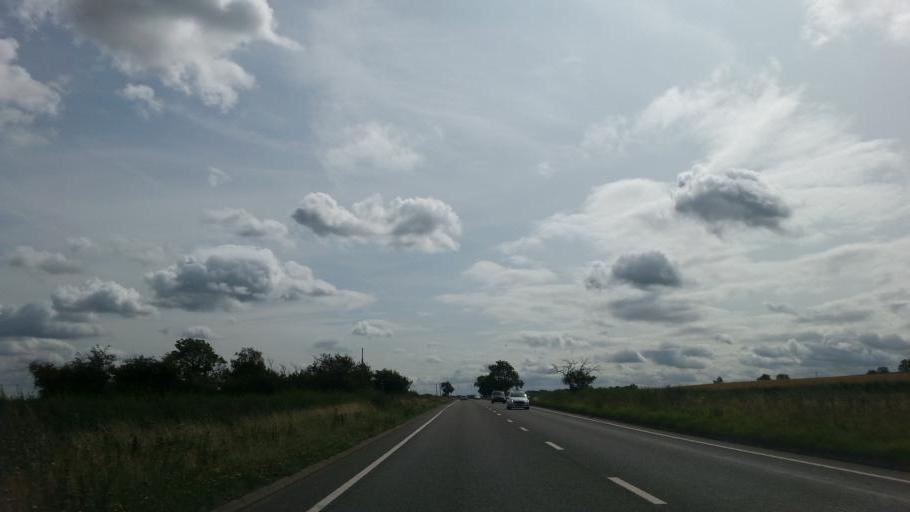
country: GB
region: England
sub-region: Leicestershire
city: Kibworth Harcourt
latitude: 52.5207
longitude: -0.9587
